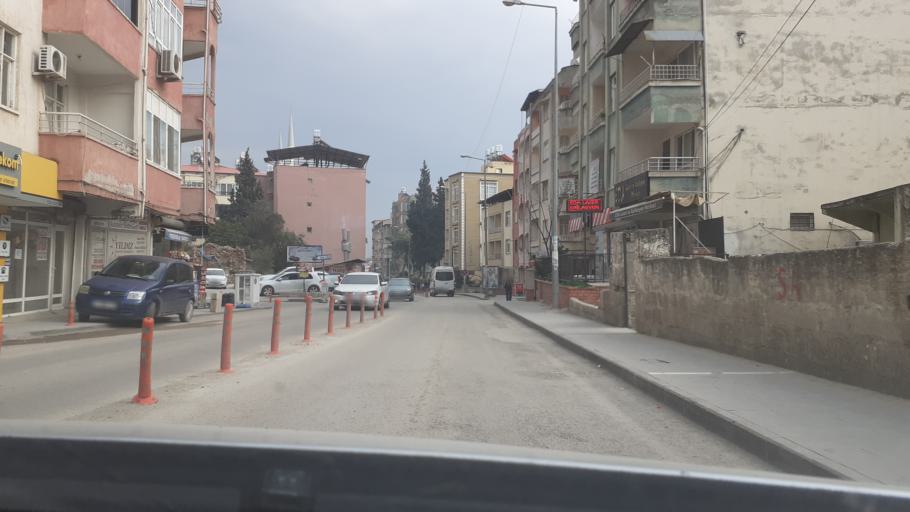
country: TR
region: Hatay
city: Kirikhan
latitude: 36.4983
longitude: 36.3522
